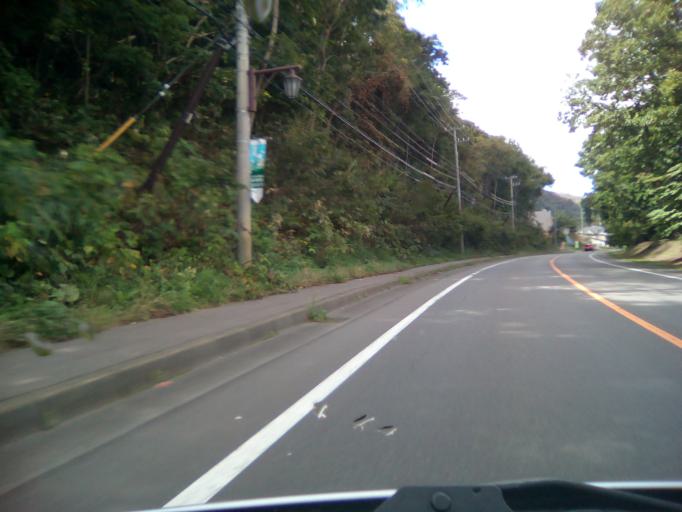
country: JP
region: Hokkaido
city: Date
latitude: 42.5667
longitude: 140.8068
